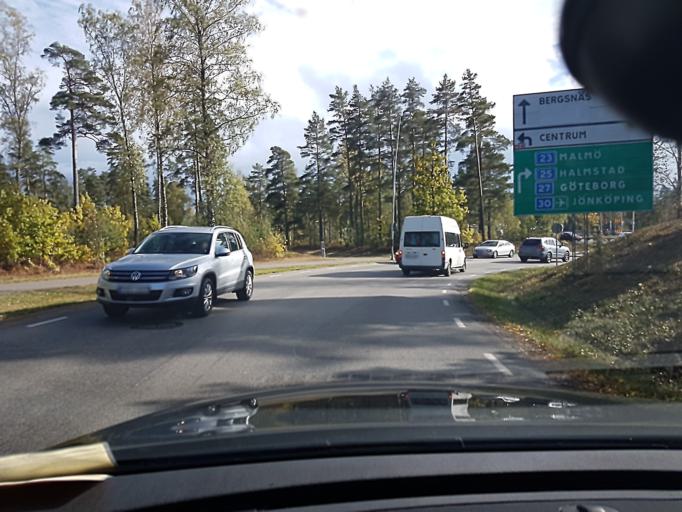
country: SE
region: Kronoberg
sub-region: Vaxjo Kommun
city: Vaexjoe
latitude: 56.8804
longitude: 14.7654
